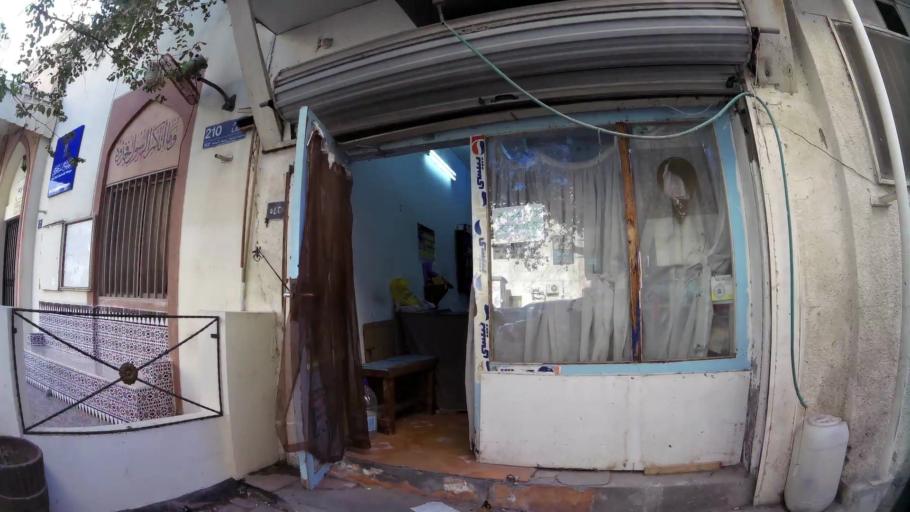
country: BH
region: Manama
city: Manama
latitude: 26.2282
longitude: 50.5752
